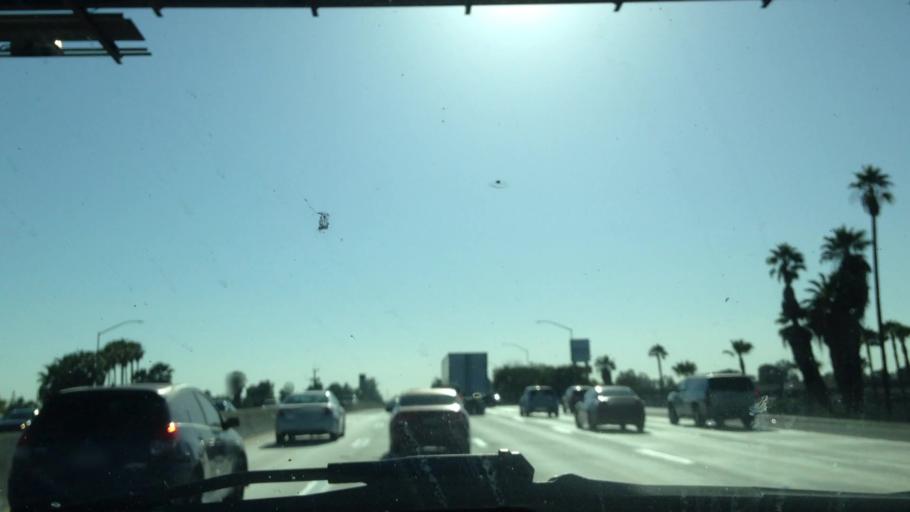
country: US
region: California
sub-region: Los Angeles County
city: Artesia
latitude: 33.8747
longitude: -118.0839
